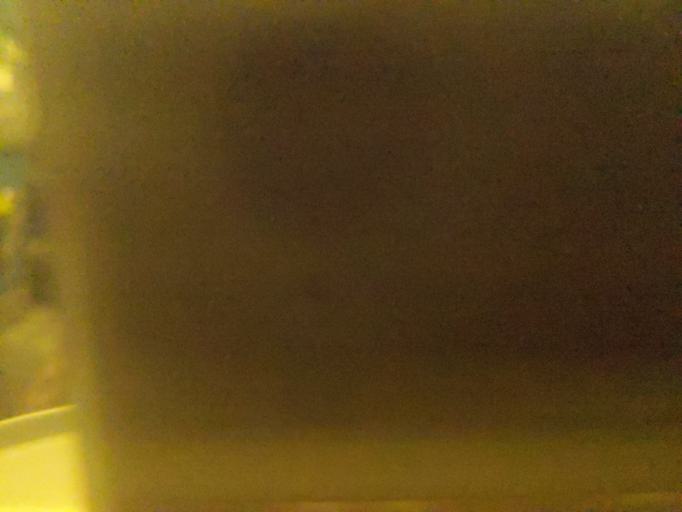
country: JP
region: Shiga Prefecture
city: Otsu-shi
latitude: 34.9751
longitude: 135.8678
